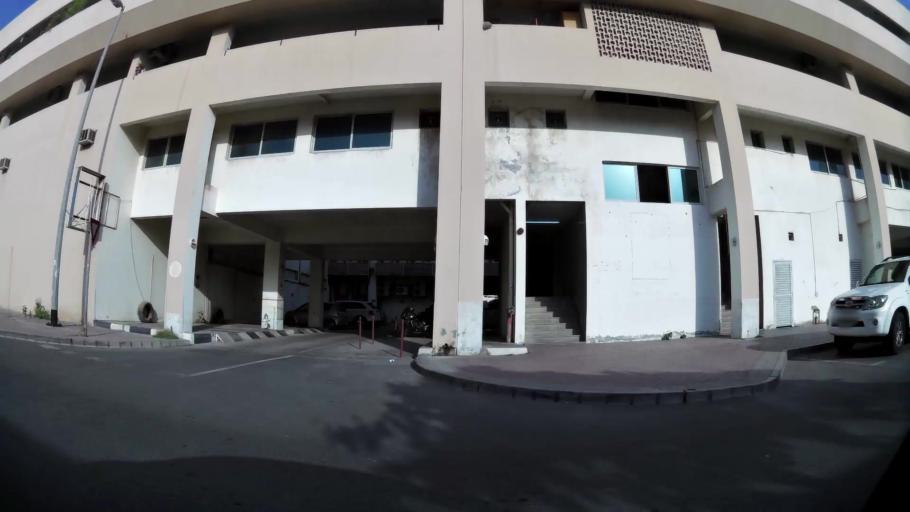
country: AE
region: Ash Shariqah
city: Sharjah
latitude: 25.2468
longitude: 55.3123
